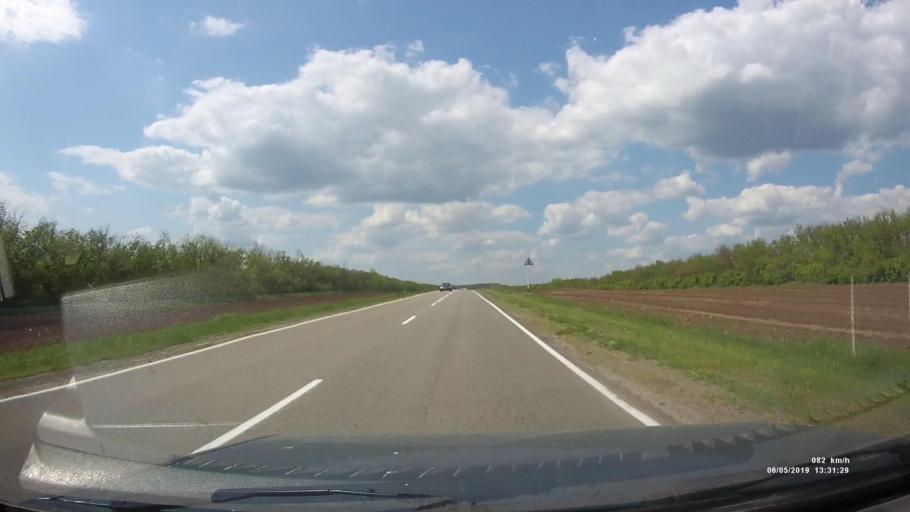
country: RU
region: Rostov
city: Ust'-Donetskiy
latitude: 47.6770
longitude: 40.8101
